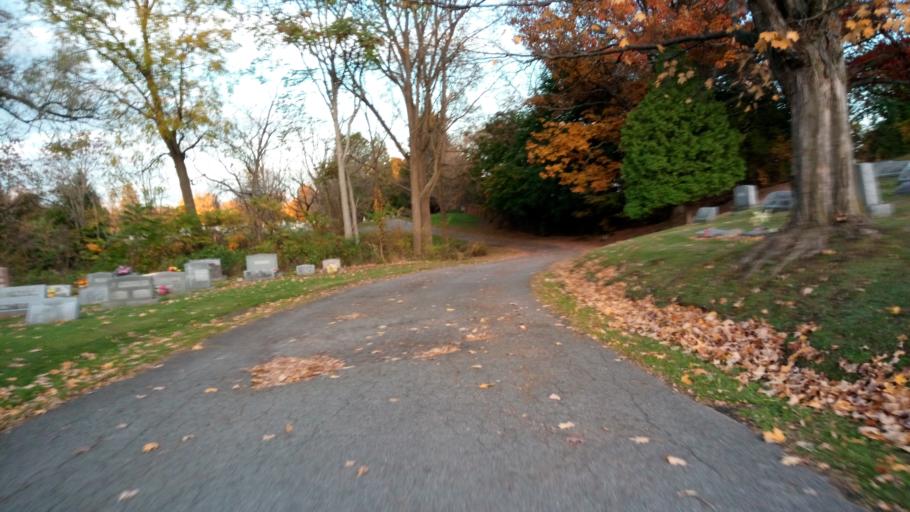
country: US
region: New York
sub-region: Chemung County
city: Southport
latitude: 42.0708
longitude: -76.8196
